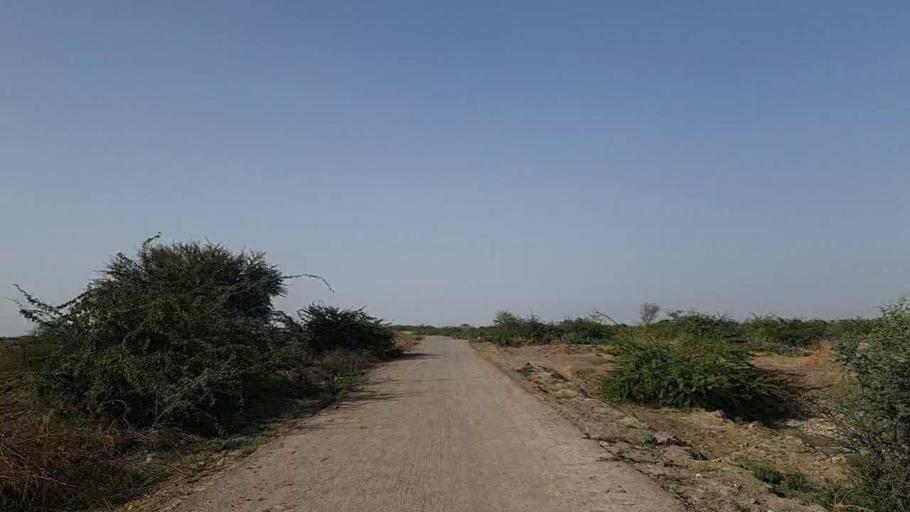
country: PK
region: Sindh
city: Jati
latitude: 24.3008
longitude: 68.1986
